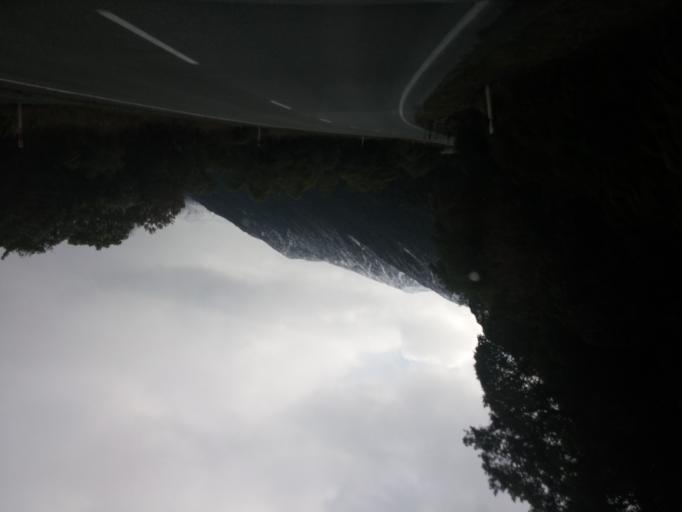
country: NZ
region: West Coast
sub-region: Grey District
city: Greymouth
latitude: -42.8176
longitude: 171.5645
